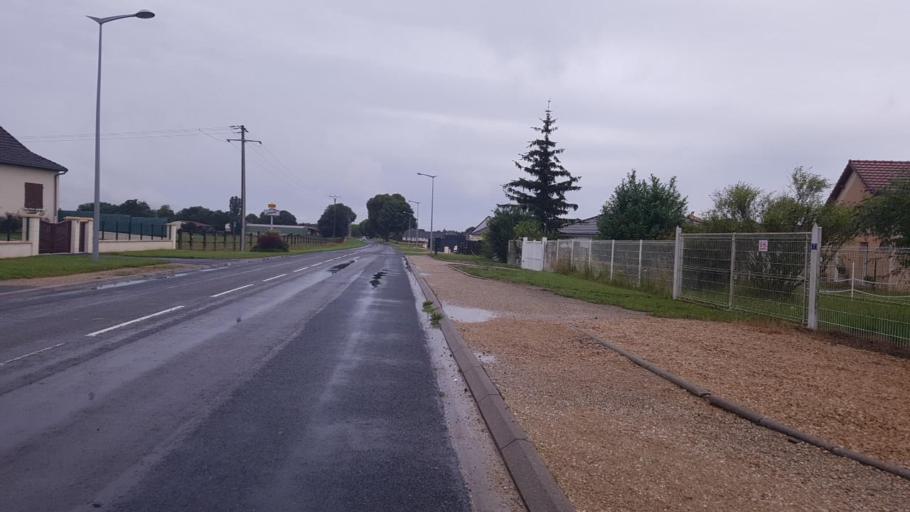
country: FR
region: Champagne-Ardenne
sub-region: Departement de la Marne
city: Sarry
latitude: 48.9023
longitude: 4.4372
